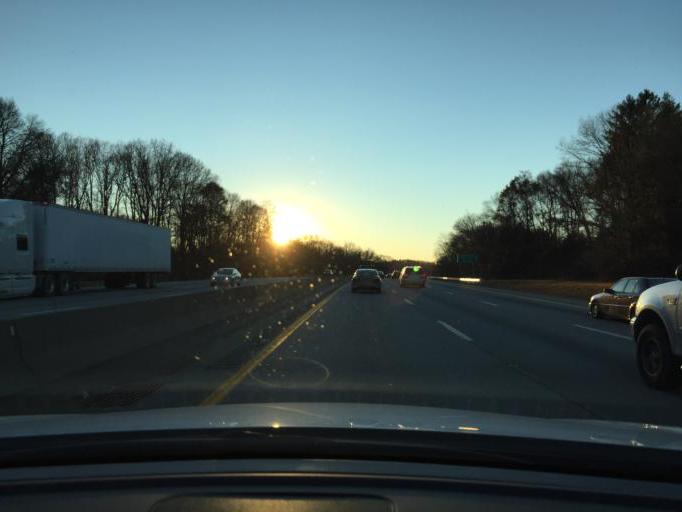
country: US
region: Massachusetts
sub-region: Middlesex County
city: Framingham Center
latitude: 42.3035
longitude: -71.4484
